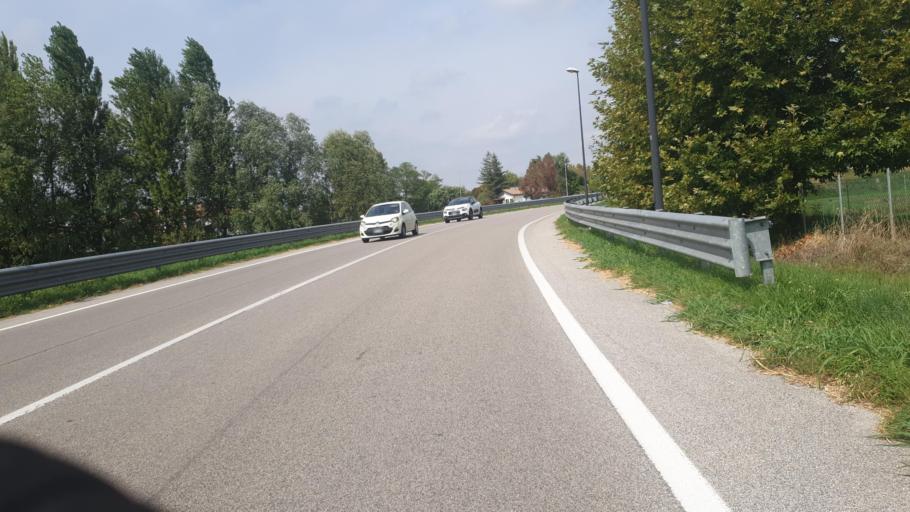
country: IT
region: Veneto
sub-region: Provincia di Padova
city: Albignasego
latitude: 45.3385
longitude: 11.8741
